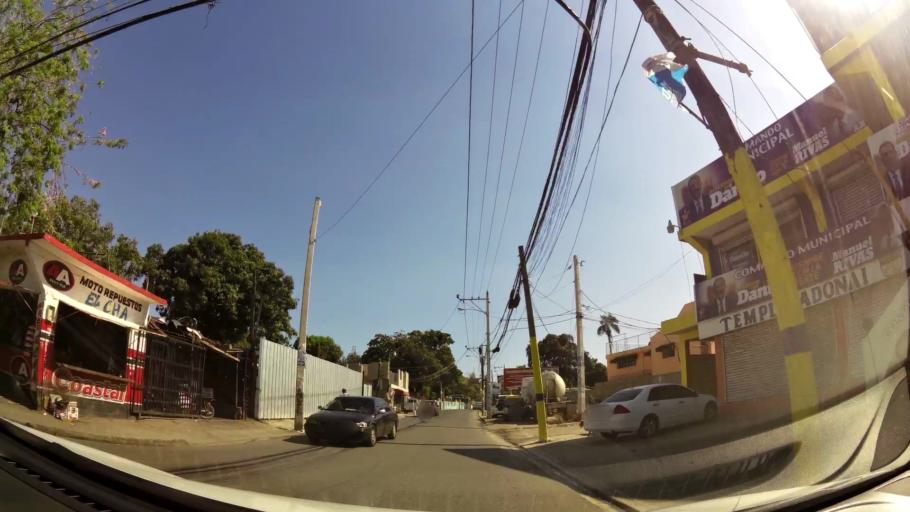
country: DO
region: Santo Domingo
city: Santo Domingo Oeste
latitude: 18.4695
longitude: -69.9989
